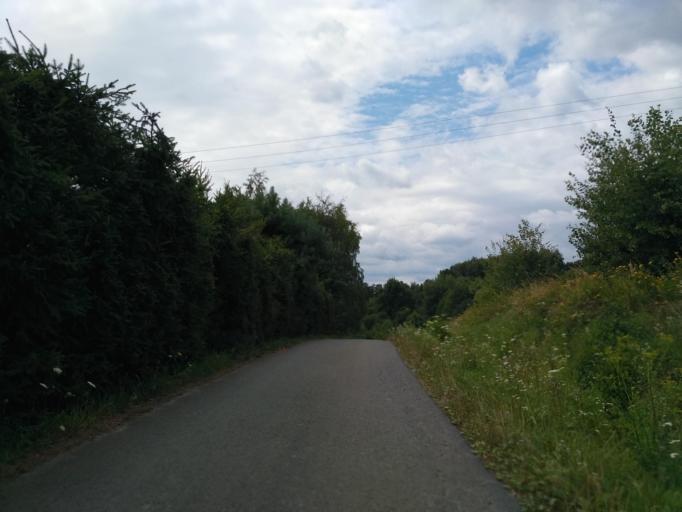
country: PL
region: Subcarpathian Voivodeship
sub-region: Powiat rzeszowski
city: Blazowa
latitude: 49.9388
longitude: 22.0899
